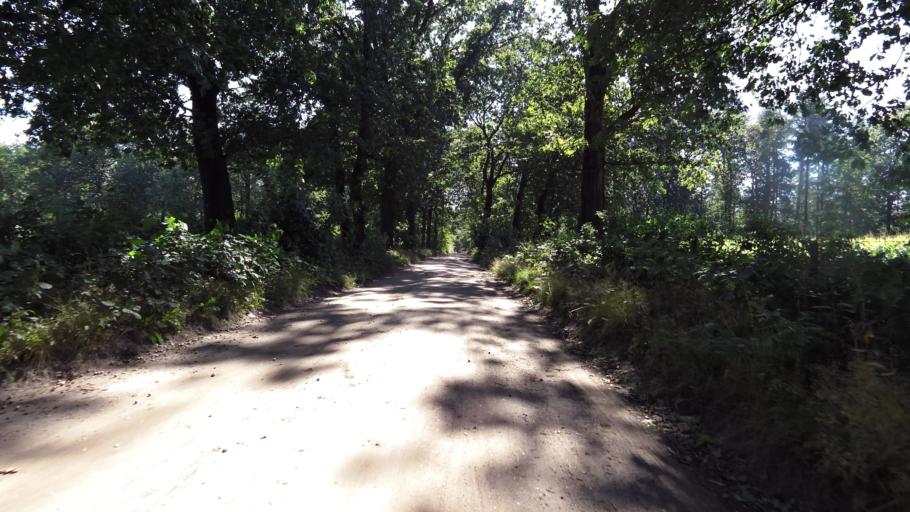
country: NL
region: Gelderland
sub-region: Gemeente Renkum
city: Renkum
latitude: 52.0000
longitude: 5.7388
